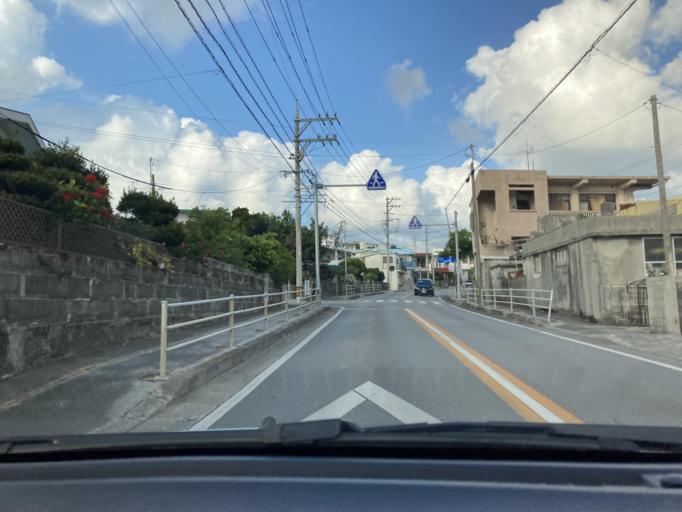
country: JP
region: Okinawa
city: Tomigusuku
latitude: 26.1494
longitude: 127.7079
